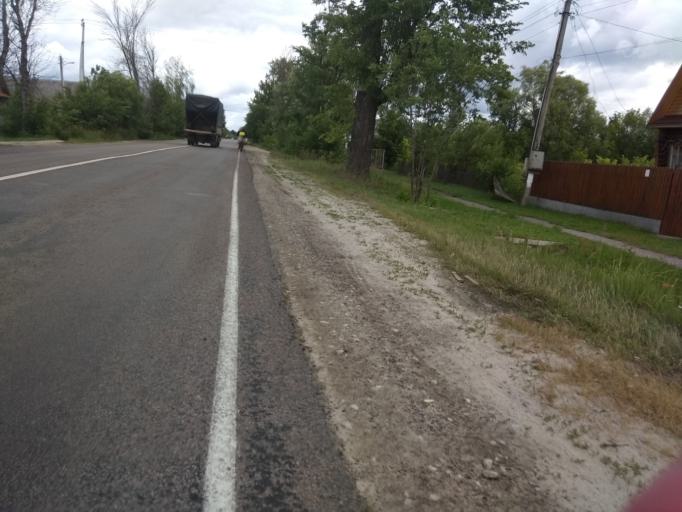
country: RU
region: Moskovskaya
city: Kerva
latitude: 55.5943
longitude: 39.7020
